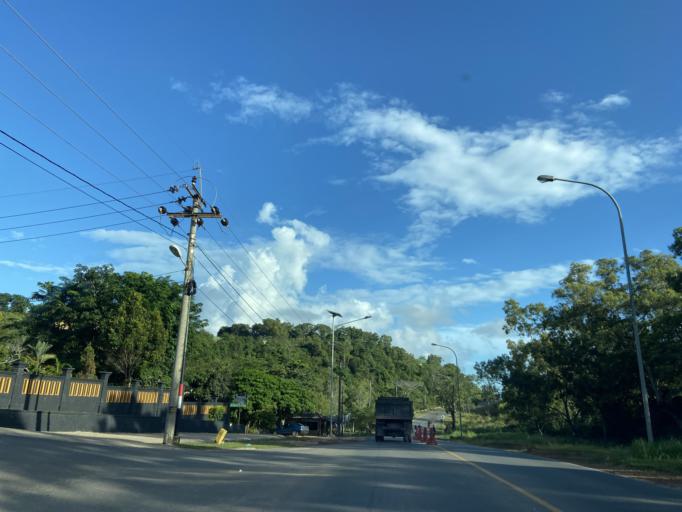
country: SG
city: Singapore
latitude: 1.0037
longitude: 104.0252
